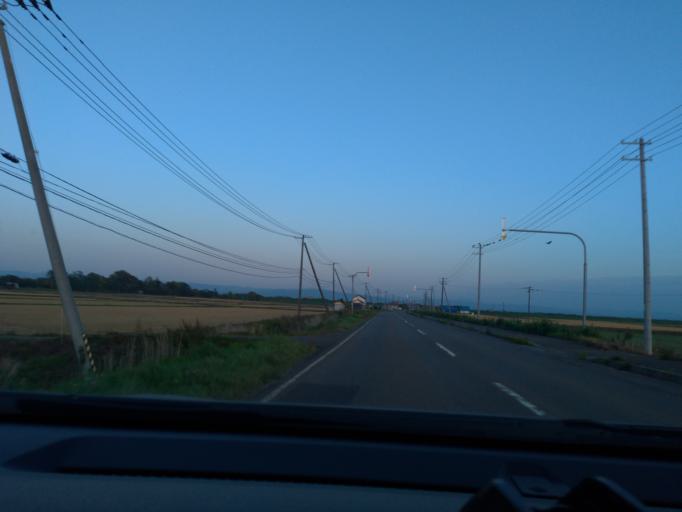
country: JP
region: Hokkaido
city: Iwamizawa
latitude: 43.3367
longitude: 141.6811
